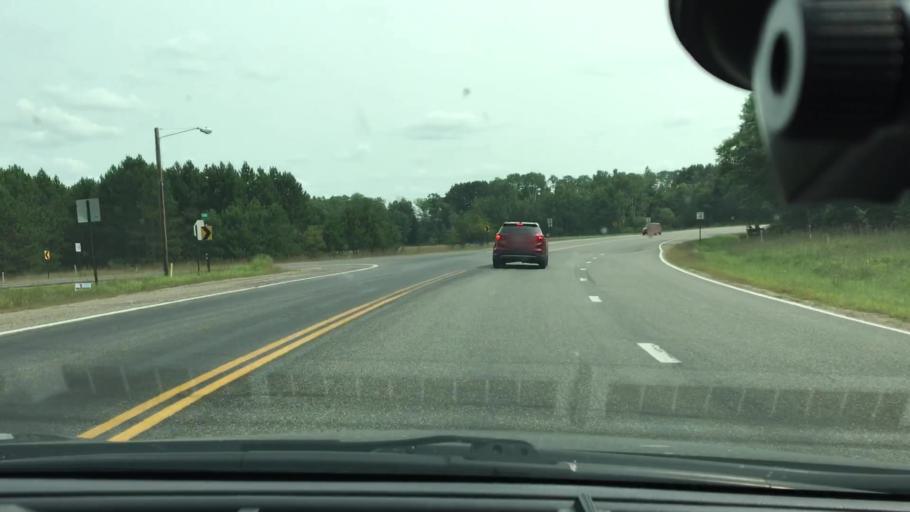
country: US
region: Minnesota
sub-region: Crow Wing County
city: Breezy Point
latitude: 46.5291
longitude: -94.1834
